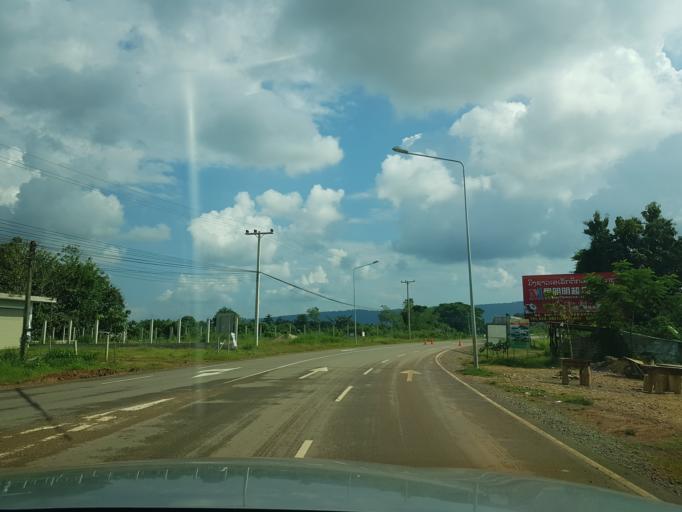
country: TH
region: Nong Khai
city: Sangkhom
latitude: 18.0907
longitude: 102.2904
